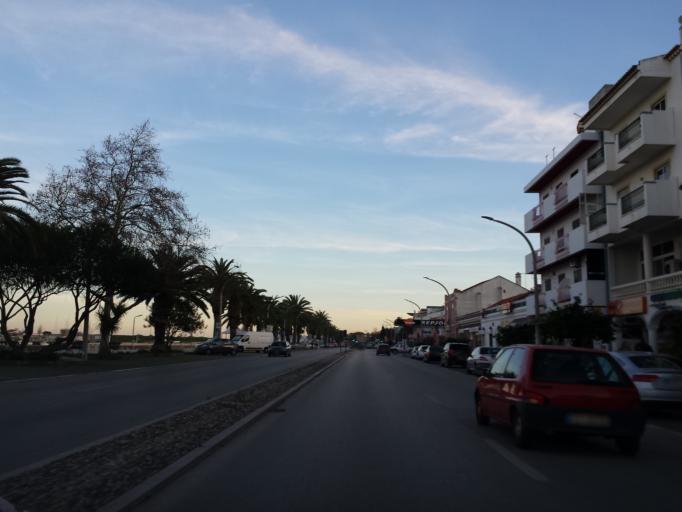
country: PT
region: Faro
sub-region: Lagos
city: Lagos
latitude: 37.1060
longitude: -8.6741
